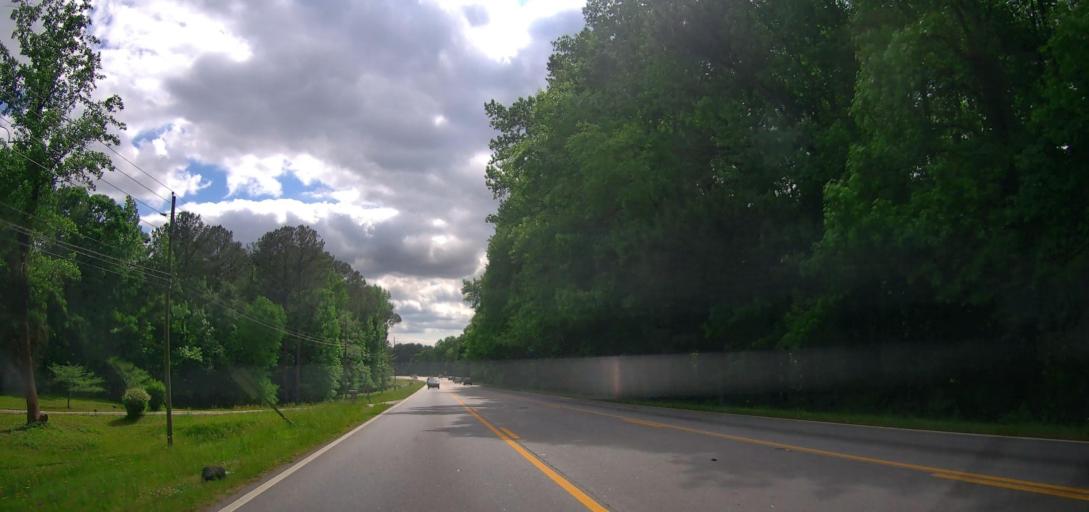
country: US
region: Georgia
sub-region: Rockdale County
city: Conyers
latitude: 33.6979
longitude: -83.9543
